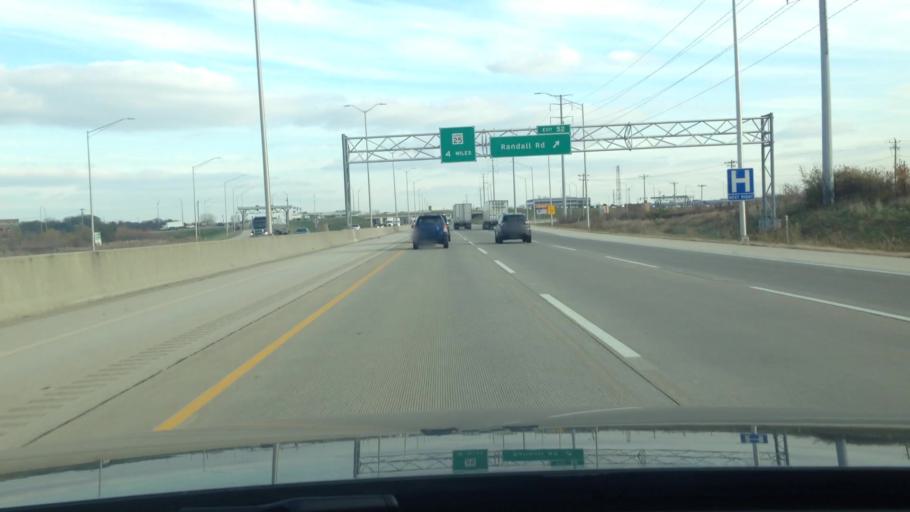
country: US
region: Illinois
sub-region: Kane County
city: Gilberts
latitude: 42.0831
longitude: -88.3412
